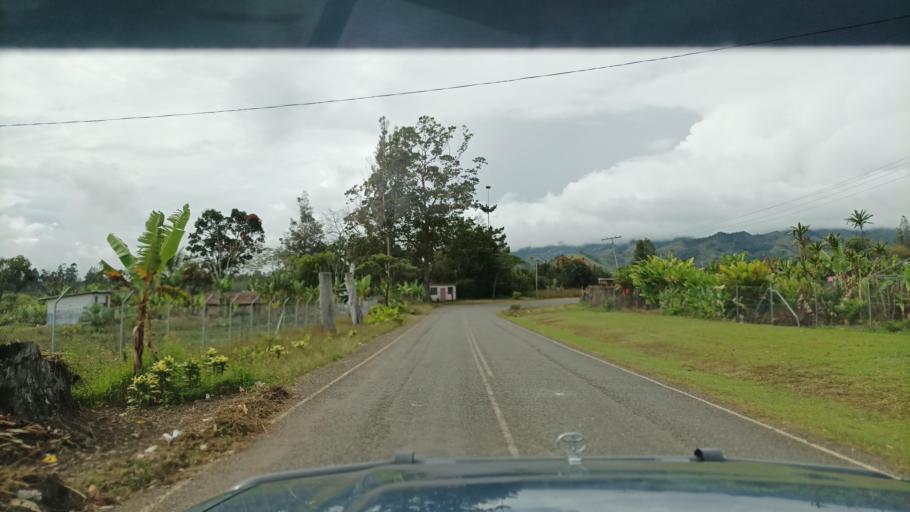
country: PG
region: Jiwaka
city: Minj
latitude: -5.9053
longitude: 144.6907
